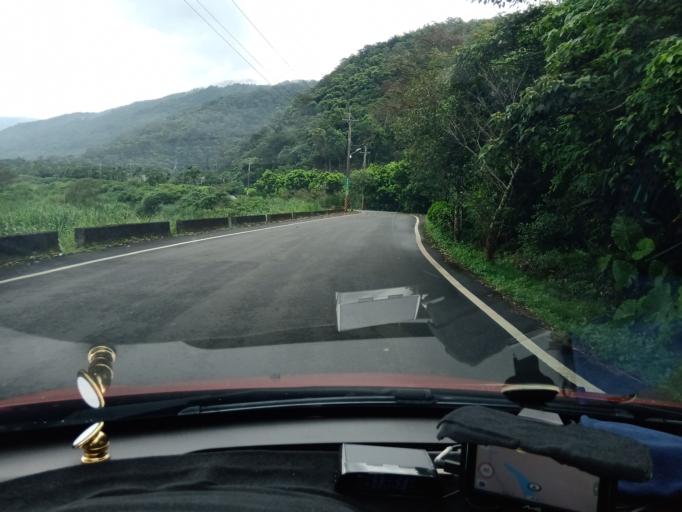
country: TW
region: Taiwan
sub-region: Yilan
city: Yilan
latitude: 24.7824
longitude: 121.7045
